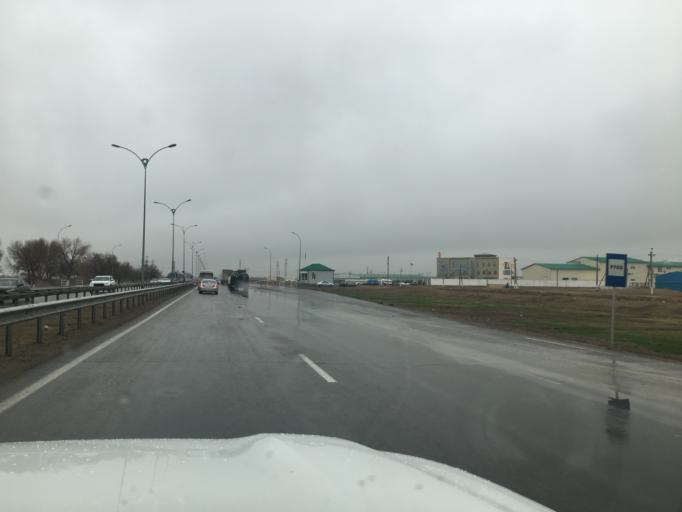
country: TM
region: Mary
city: Mary
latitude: 37.5479
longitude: 61.7466
